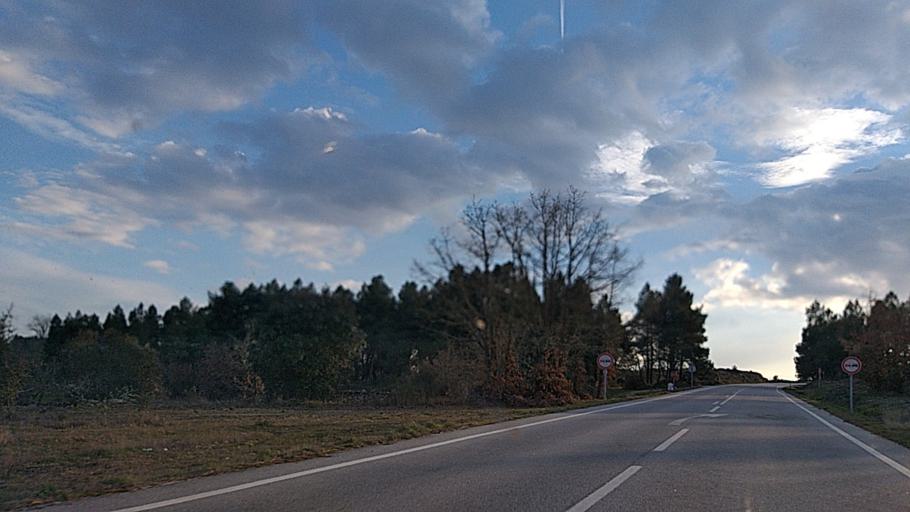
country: PT
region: Guarda
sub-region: Pinhel
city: Pinhel
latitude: 40.6713
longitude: -6.9531
